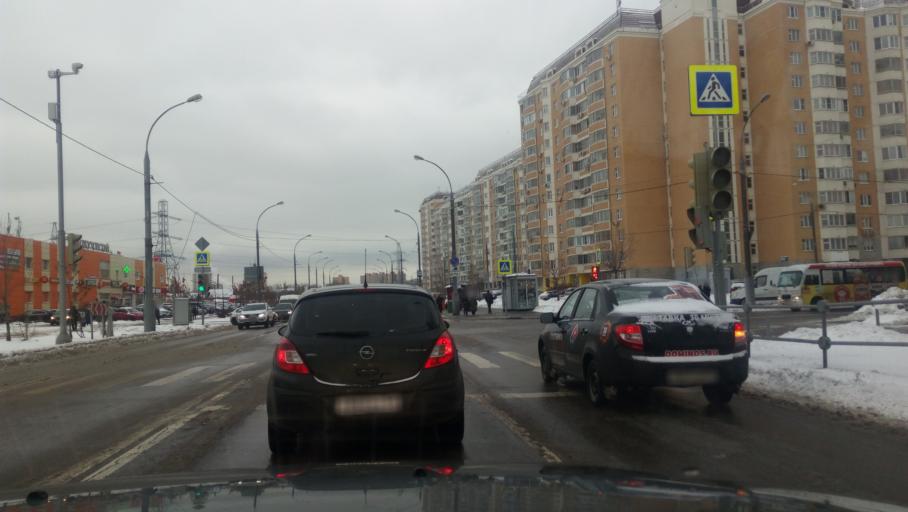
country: RU
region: Moscow
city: Nekrasovka
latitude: 55.7128
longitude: 37.8982
